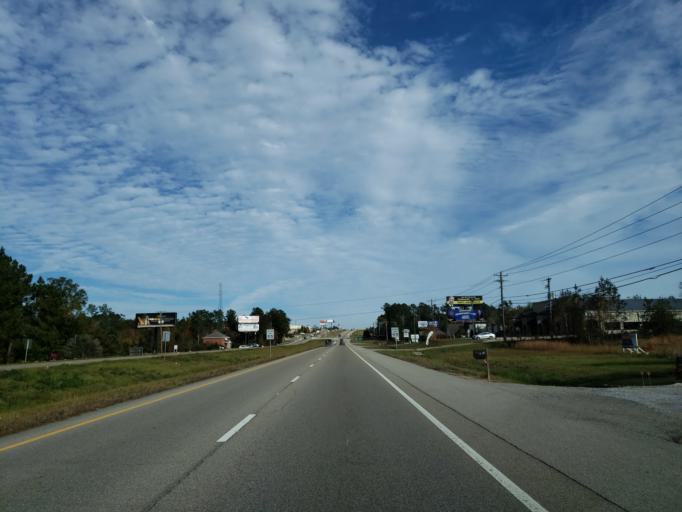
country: US
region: Mississippi
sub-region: Lamar County
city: West Hattiesburg
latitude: 31.3167
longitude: -89.4262
